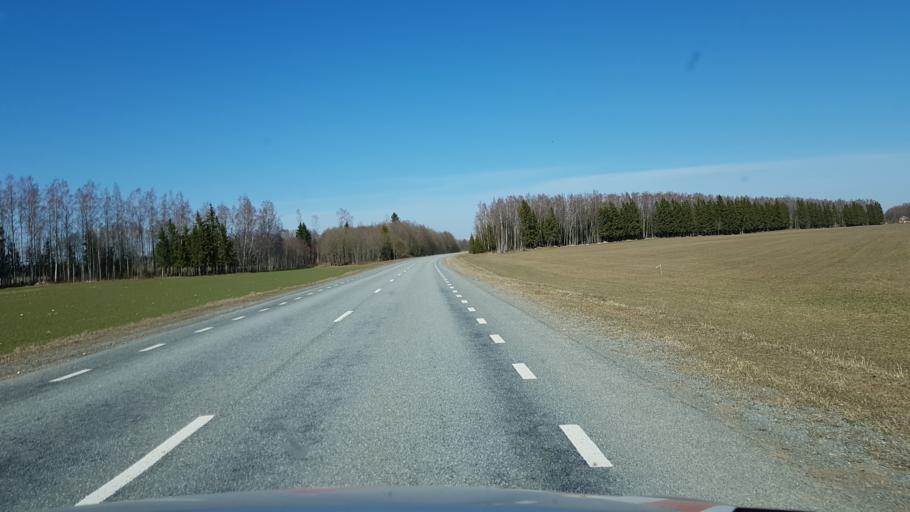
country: EE
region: Jaervamaa
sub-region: Jaerva-Jaani vald
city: Jarva-Jaani
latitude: 59.0925
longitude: 25.9782
